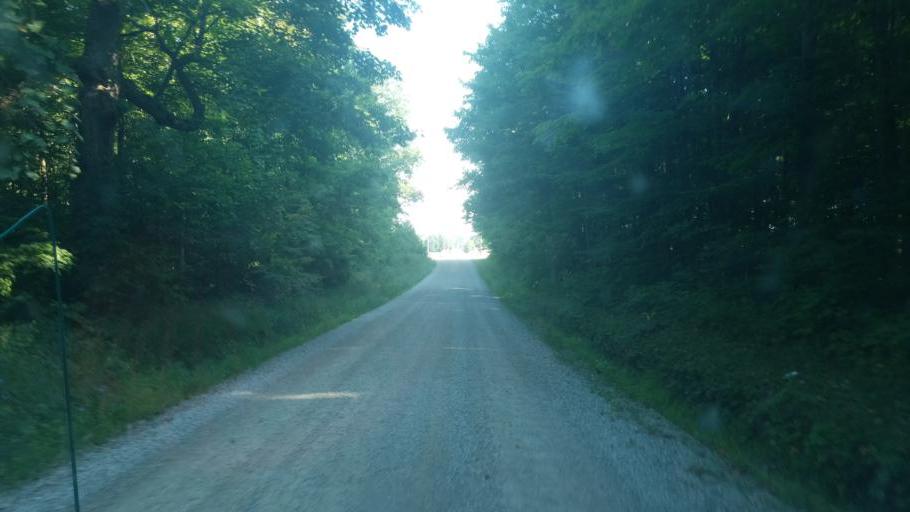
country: US
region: Ohio
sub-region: Ashland County
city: Ashland
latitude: 40.9659
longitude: -82.3402
